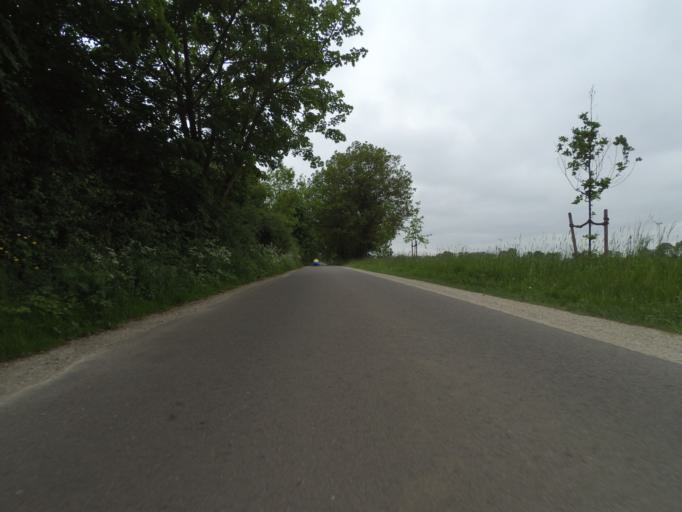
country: DE
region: Lower Saxony
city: Uetze
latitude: 52.4826
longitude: 10.1990
